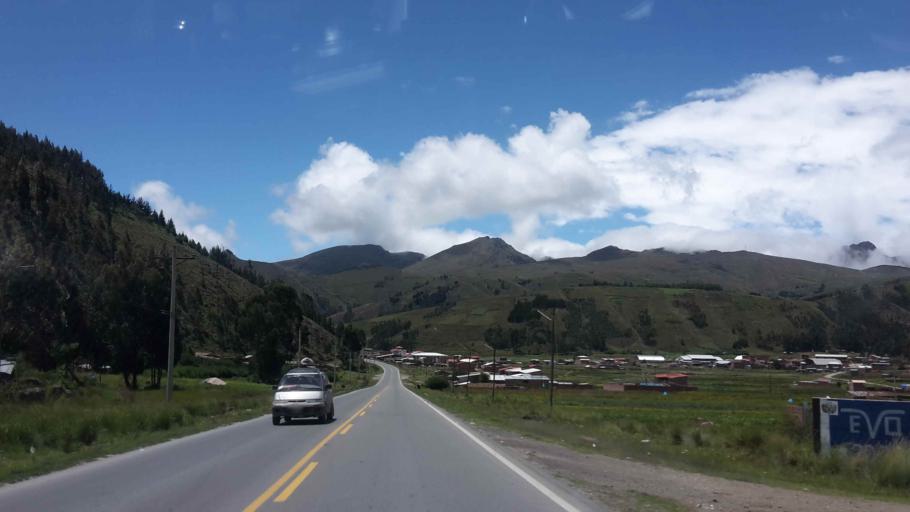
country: BO
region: Cochabamba
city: Colomi
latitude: -17.3802
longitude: -65.8344
